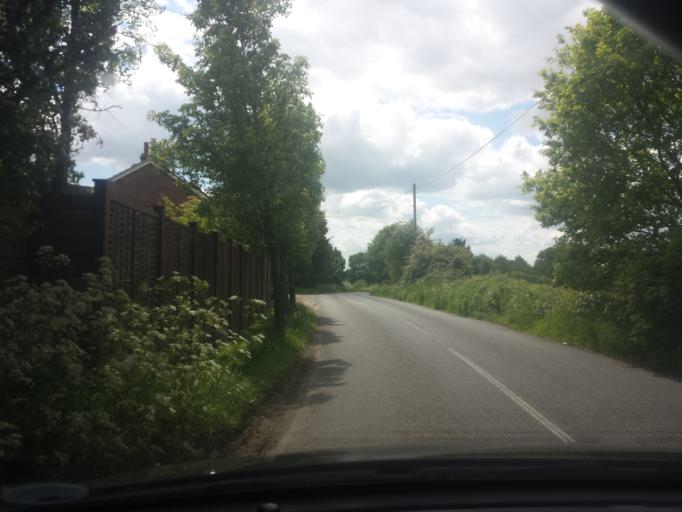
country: GB
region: England
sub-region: Essex
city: Little Clacton
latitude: 51.8751
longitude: 1.1461
